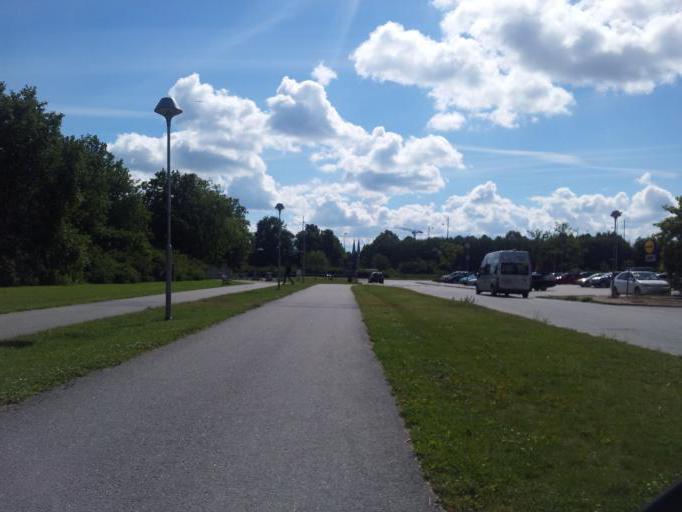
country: SE
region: Uppsala
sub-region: Uppsala Kommun
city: Uppsala
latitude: 59.8709
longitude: 17.6578
